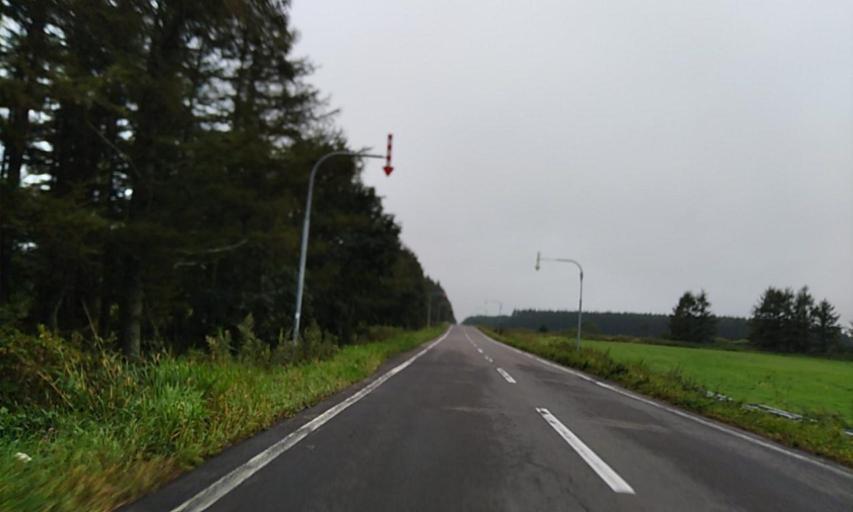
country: JP
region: Hokkaido
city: Shibetsu
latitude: 43.5242
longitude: 144.6908
